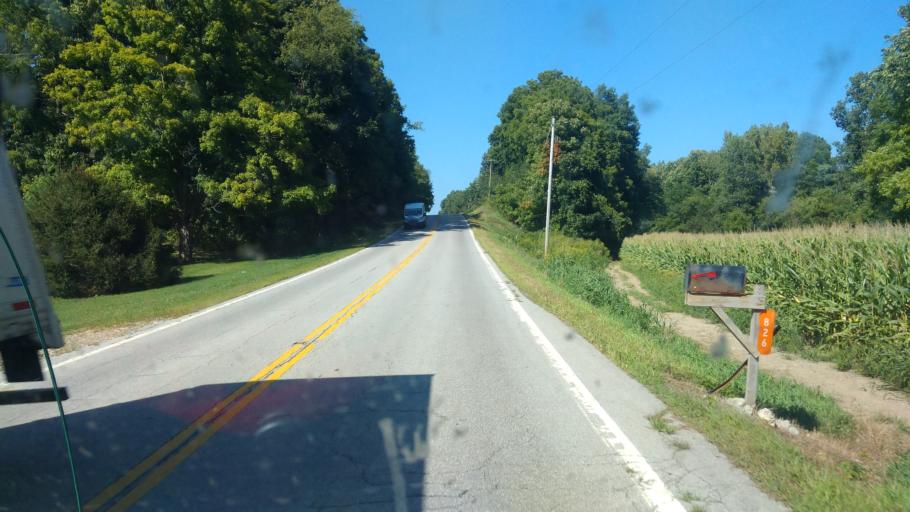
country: US
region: Ohio
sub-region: Ashland County
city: Ashland
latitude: 40.9403
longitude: -82.2668
